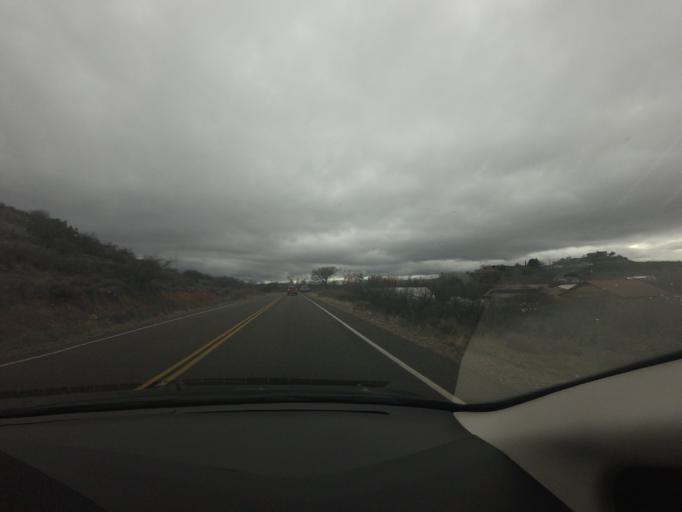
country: US
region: Arizona
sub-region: Yavapai County
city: Lake Montezuma
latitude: 34.6500
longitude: -111.7658
